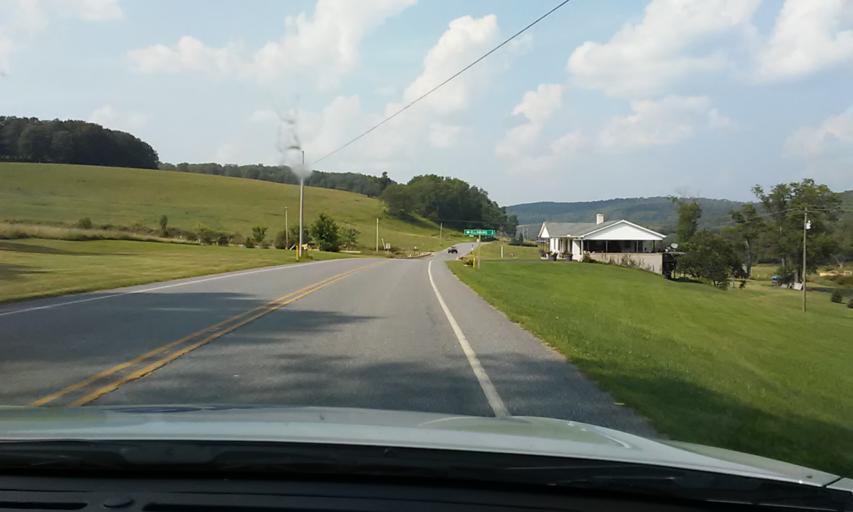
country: US
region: New York
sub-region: Allegany County
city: Wellsville
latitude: 41.9251
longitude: -77.8546
